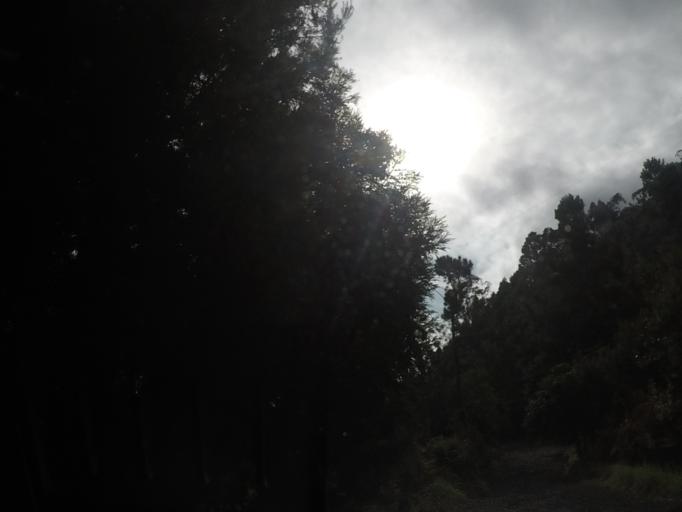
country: PT
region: Madeira
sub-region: Sao Vicente
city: Sao Vicente
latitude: 32.7800
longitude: -17.0500
